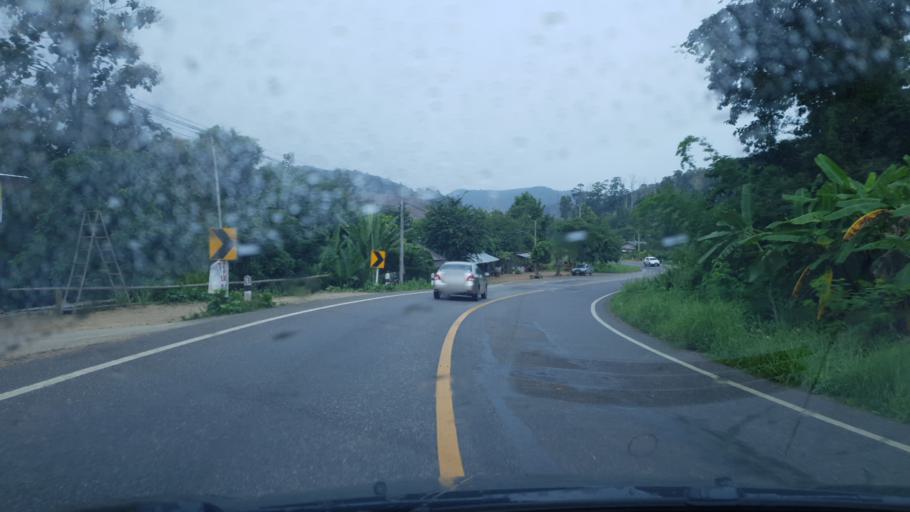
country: TH
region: Mae Hong Son
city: Khun Yuam
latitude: 18.6984
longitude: 97.9186
